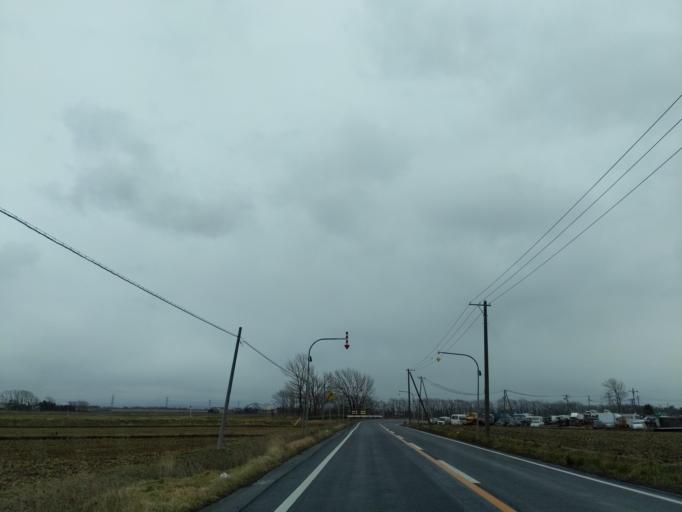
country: JP
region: Hokkaido
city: Ebetsu
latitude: 43.0987
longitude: 141.6205
